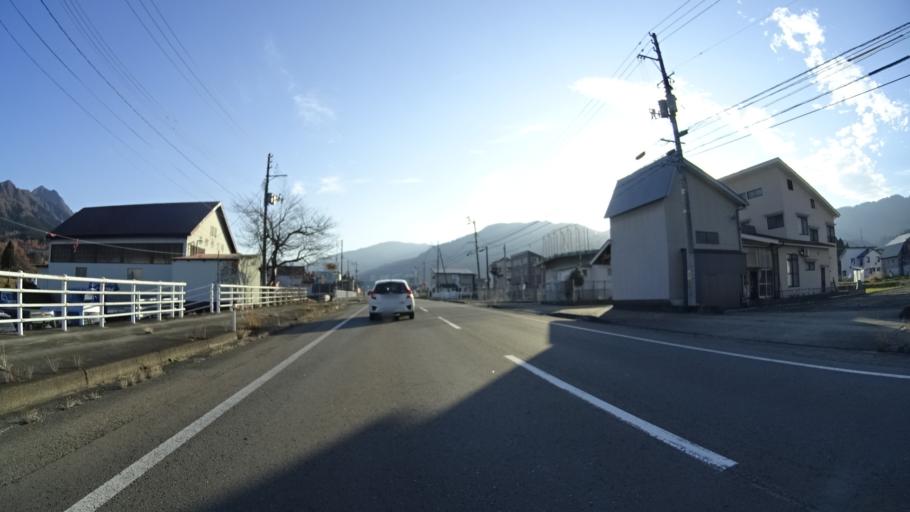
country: JP
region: Niigata
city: Shiozawa
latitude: 36.9881
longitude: 138.8091
